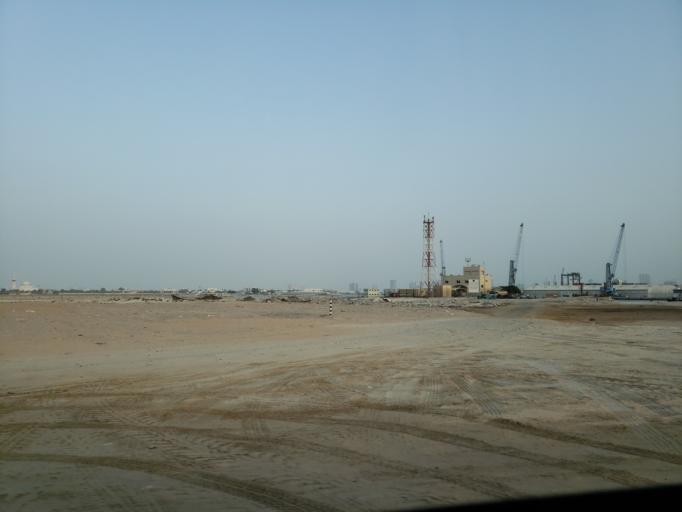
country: AE
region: Ajman
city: Ajman
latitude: 25.4275
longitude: 55.4525
